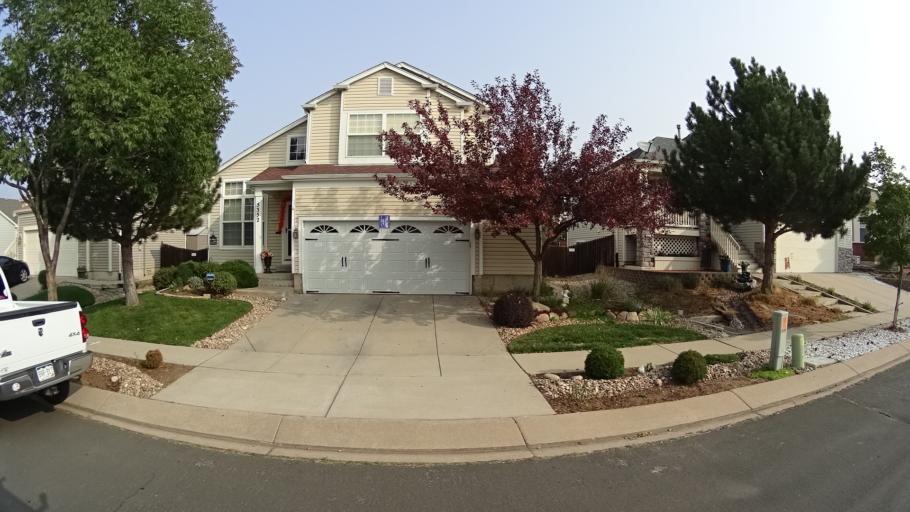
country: US
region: Colorado
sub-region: El Paso County
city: Cimarron Hills
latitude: 38.9301
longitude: -104.7302
